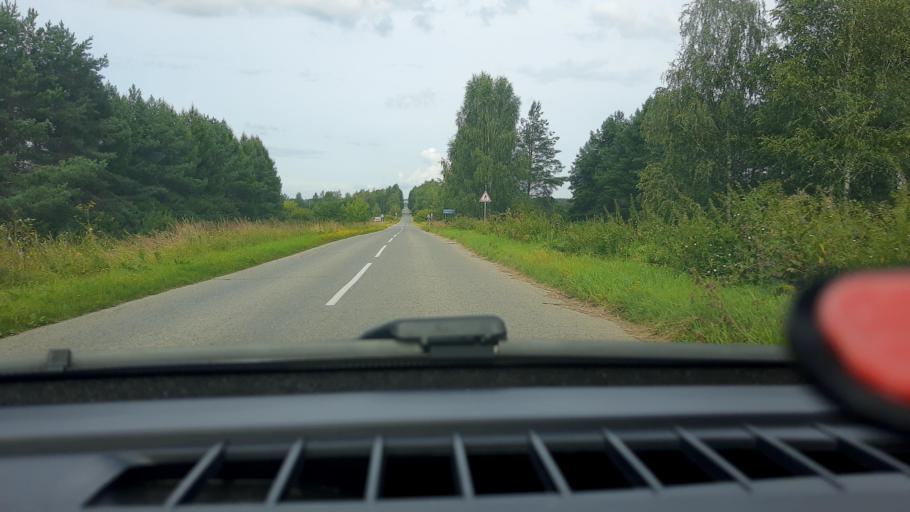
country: RU
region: Nizjnij Novgorod
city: Burevestnik
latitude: 56.0491
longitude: 43.7026
